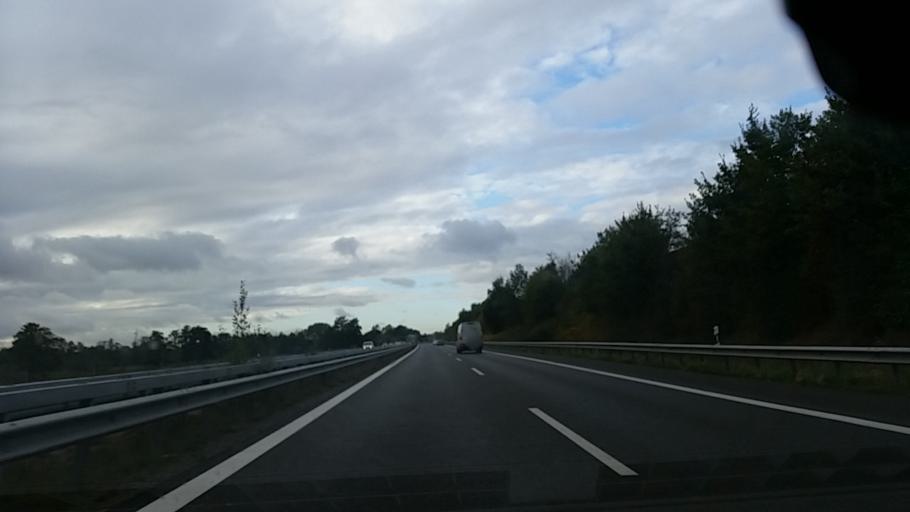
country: DE
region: Schleswig-Holstein
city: Bornsen
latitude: 53.4671
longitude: 10.2690
